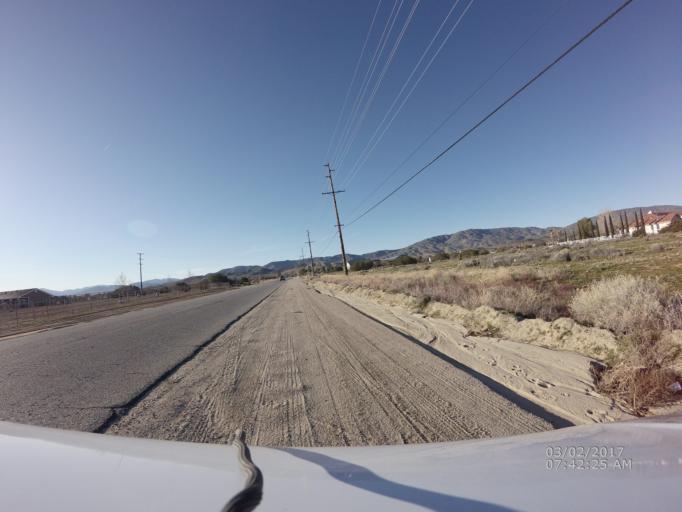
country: US
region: California
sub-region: Los Angeles County
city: Desert View Highlands
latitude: 34.6063
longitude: -118.1656
